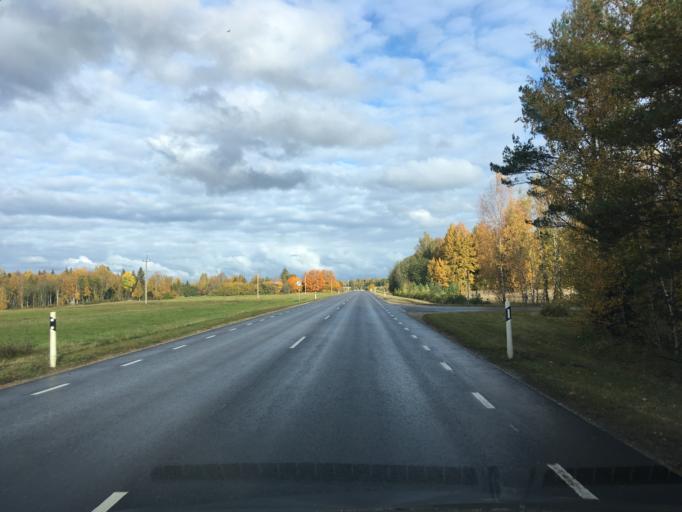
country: EE
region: Harju
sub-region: Raasiku vald
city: Raasiku
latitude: 59.1978
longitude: 25.1843
